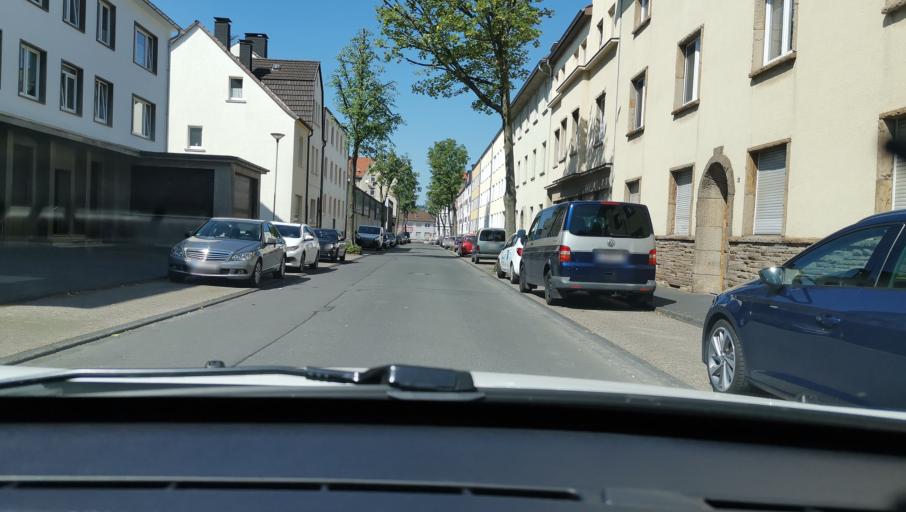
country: DE
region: North Rhine-Westphalia
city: Herdecke
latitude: 51.3838
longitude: 7.4540
